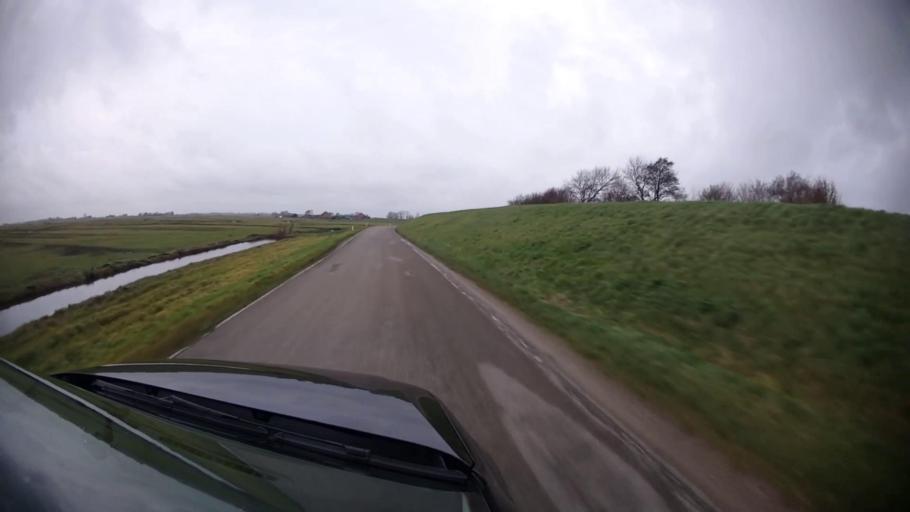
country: NL
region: North Holland
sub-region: Gemeente Waterland
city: Marken
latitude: 52.4243
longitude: 5.0727
